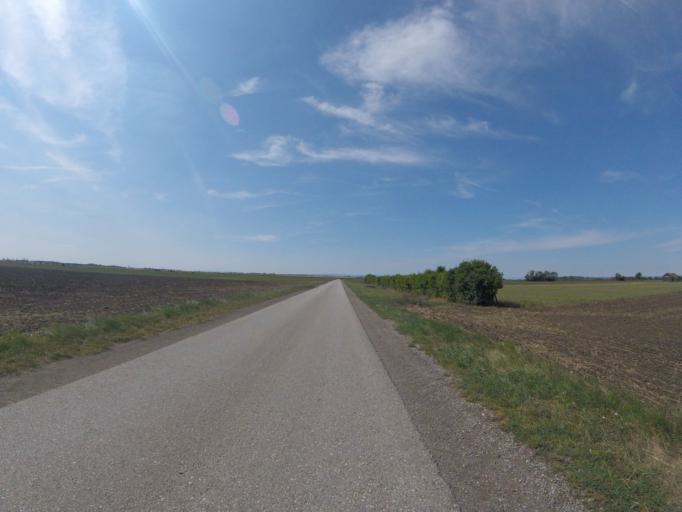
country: AT
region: Burgenland
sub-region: Politischer Bezirk Neusiedl am See
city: Frauenkirchen
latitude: 47.8227
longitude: 16.8879
